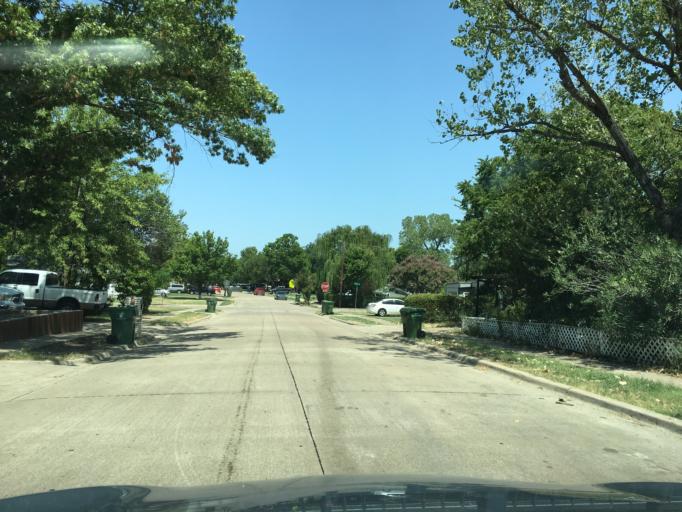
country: US
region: Texas
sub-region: Dallas County
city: Garland
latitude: 32.8963
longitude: -96.6261
